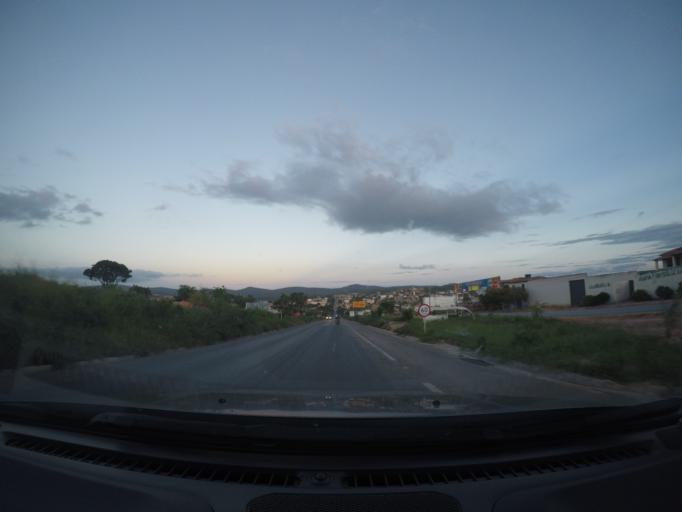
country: BR
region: Bahia
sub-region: Seabra
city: Seabra
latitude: -12.4295
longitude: -41.7825
